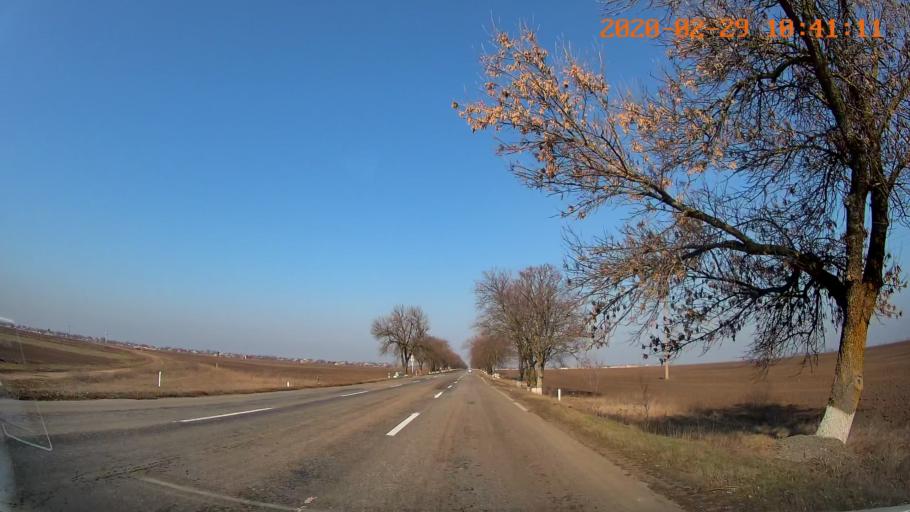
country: MD
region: Telenesti
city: Grigoriopol
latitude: 47.0401
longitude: 29.4287
